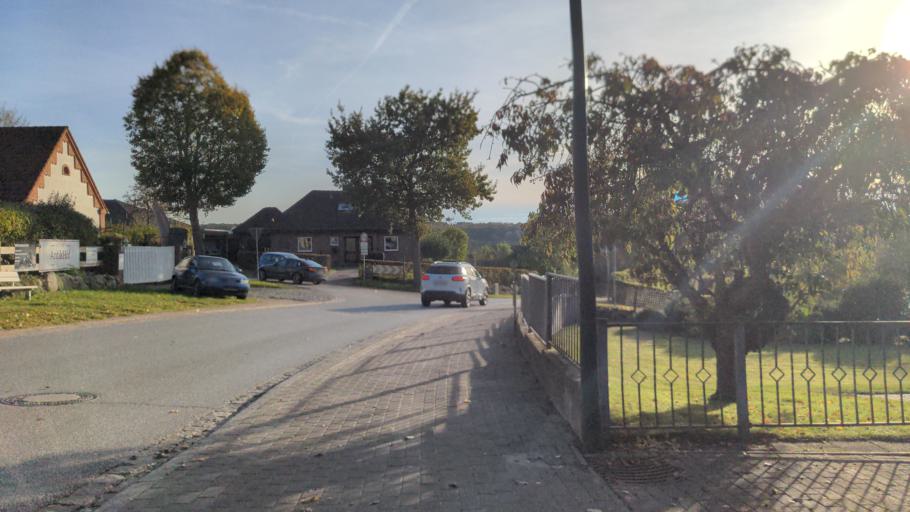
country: DE
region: Schleswig-Holstein
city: Kirchnuchel
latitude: 54.1988
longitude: 10.6503
